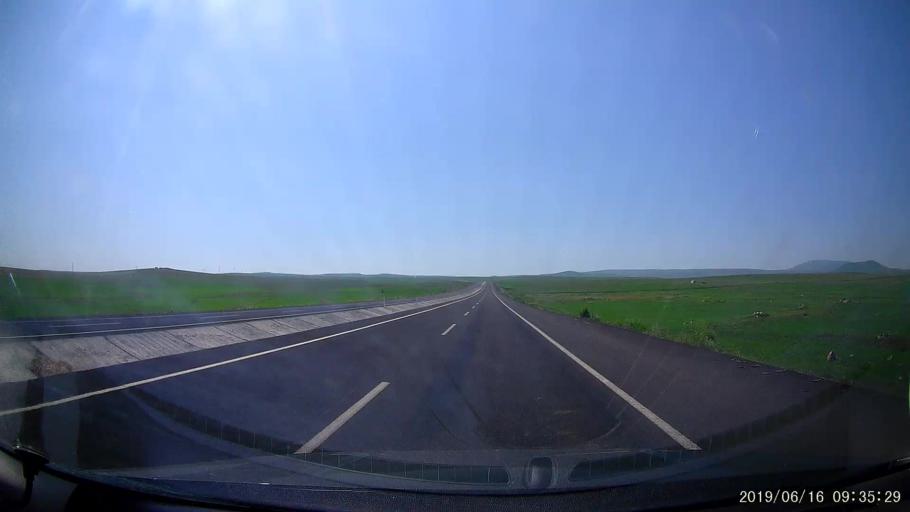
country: TR
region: Kars
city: Kars
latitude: 40.5712
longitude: 43.1568
